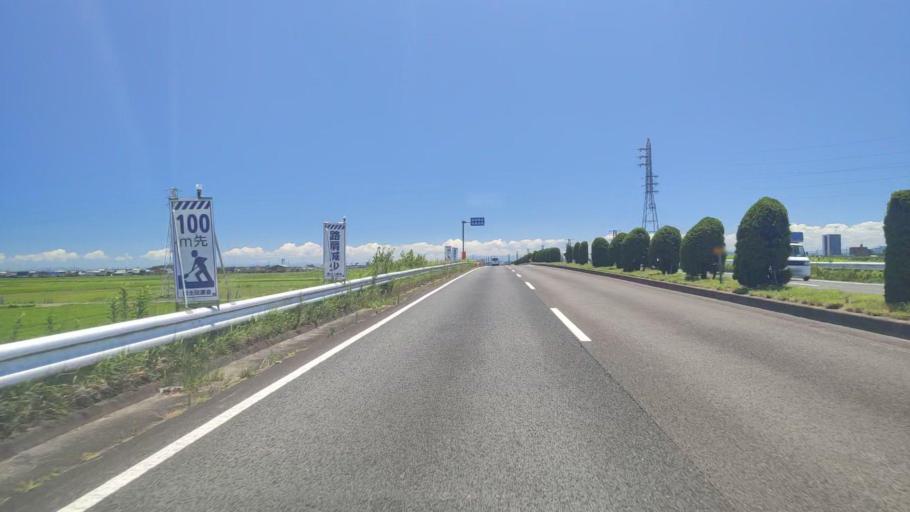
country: JP
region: Mie
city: Suzuka
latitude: 34.8946
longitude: 136.6023
